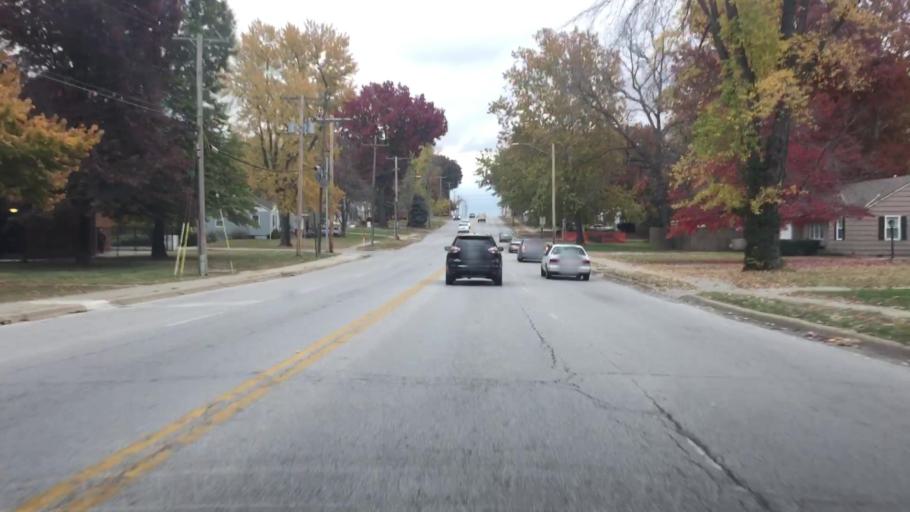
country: US
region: Missouri
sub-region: Jackson County
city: Raytown
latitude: 38.9951
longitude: -94.4813
